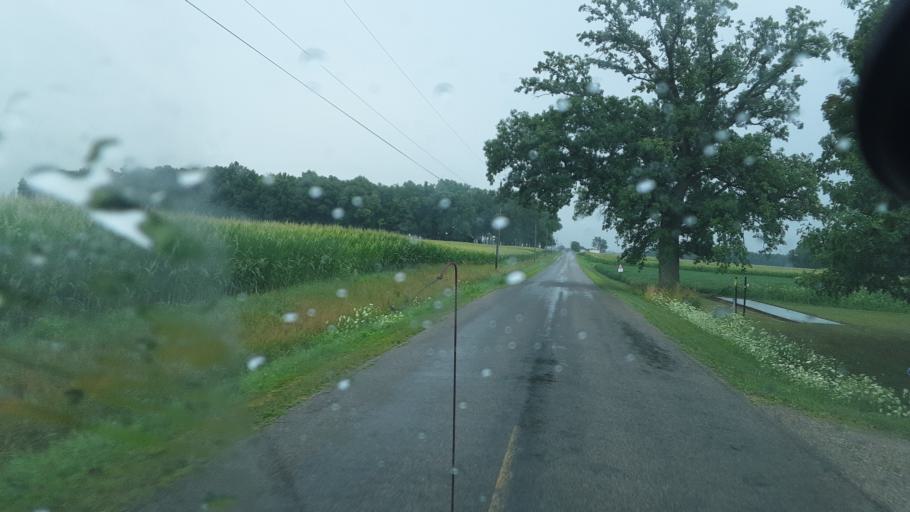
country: US
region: Ohio
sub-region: Williams County
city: Edgerton
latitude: 41.5051
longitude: -84.7880
